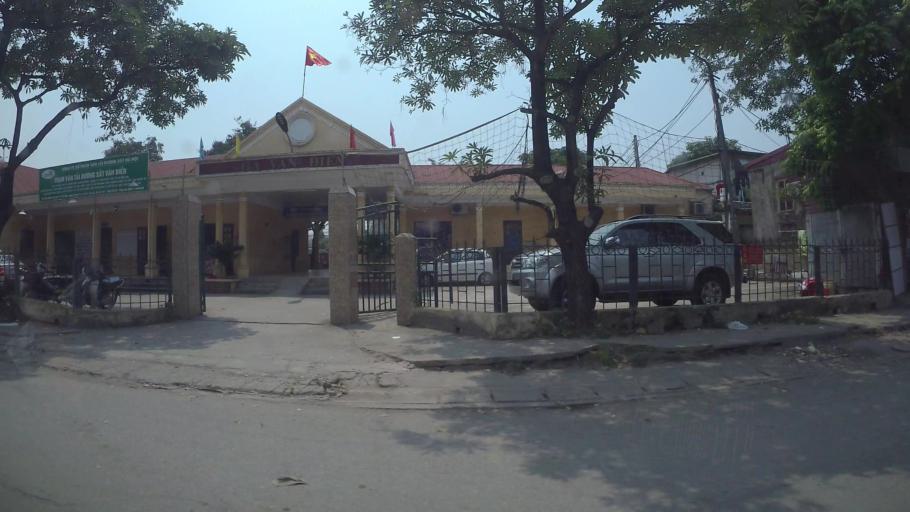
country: VN
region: Ha Noi
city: Van Dien
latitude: 20.9444
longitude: 105.8443
